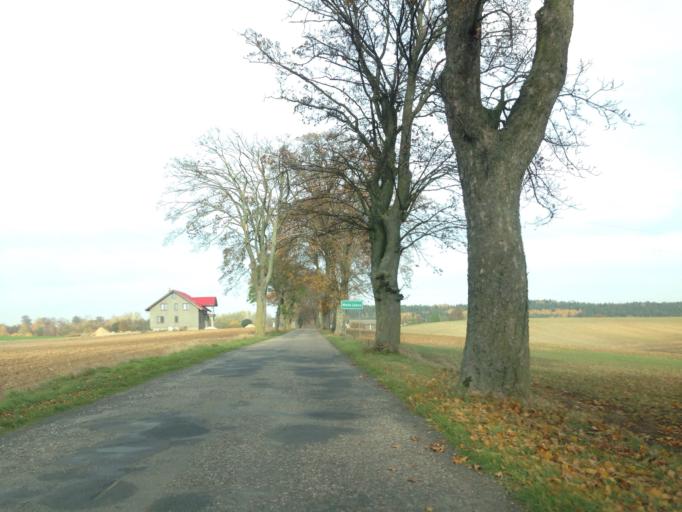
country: PL
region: Kujawsko-Pomorskie
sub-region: Powiat brodnicki
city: Bartniczka
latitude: 53.2810
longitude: 19.6906
